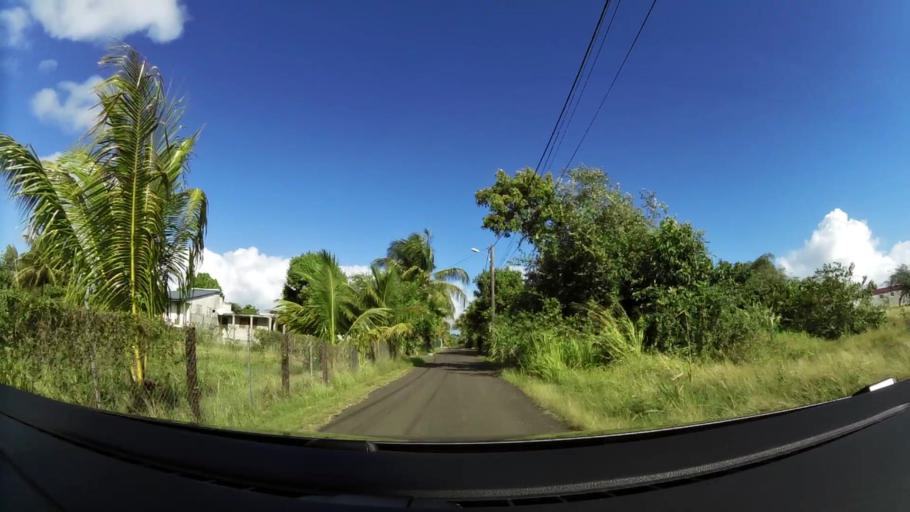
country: GP
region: Guadeloupe
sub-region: Guadeloupe
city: Petit-Canal
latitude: 16.3694
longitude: -61.4656
